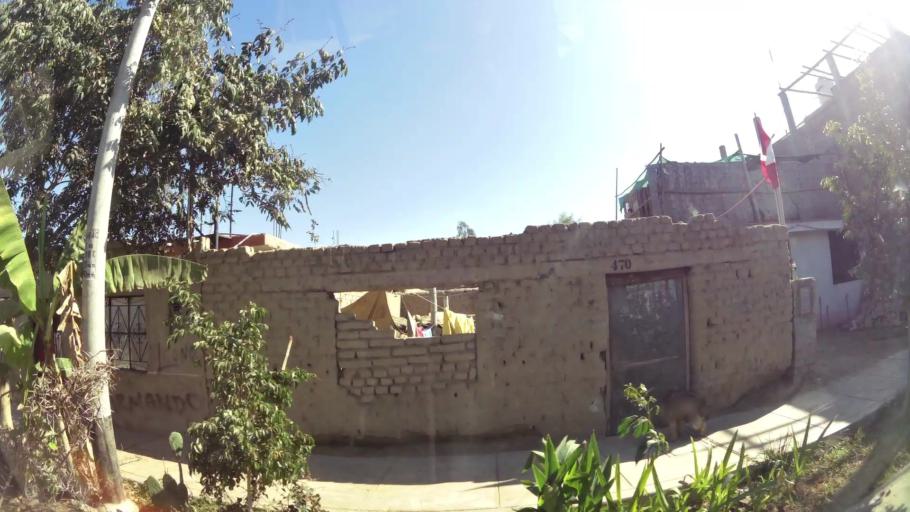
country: PE
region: Ica
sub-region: Provincia de Ica
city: La Tinguina
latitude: -14.0448
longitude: -75.7097
